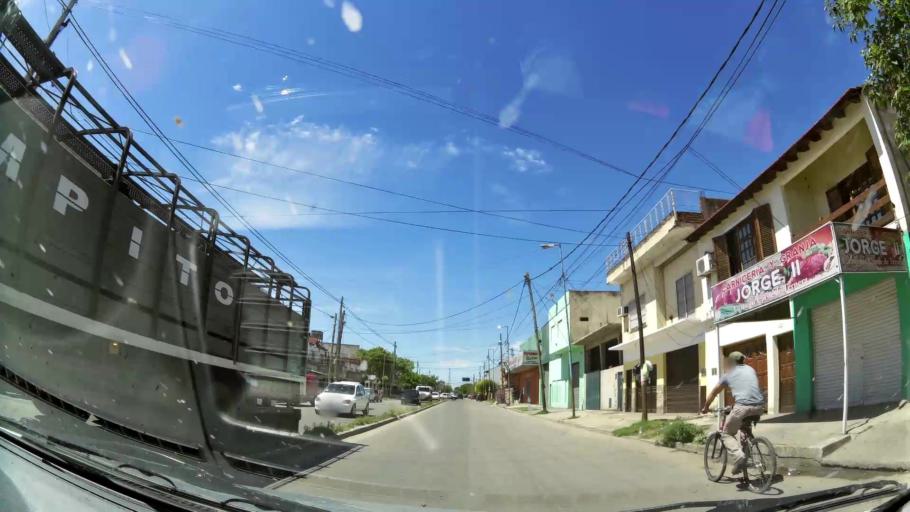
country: AR
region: Buenos Aires
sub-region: Partido de Quilmes
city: Quilmes
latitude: -34.7319
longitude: -58.3057
